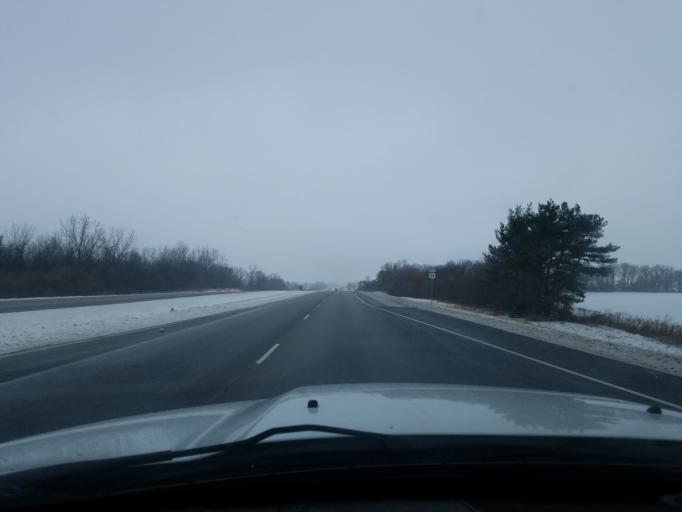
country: US
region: Indiana
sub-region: Fulton County
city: Rochester
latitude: 40.9388
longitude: -86.1683
